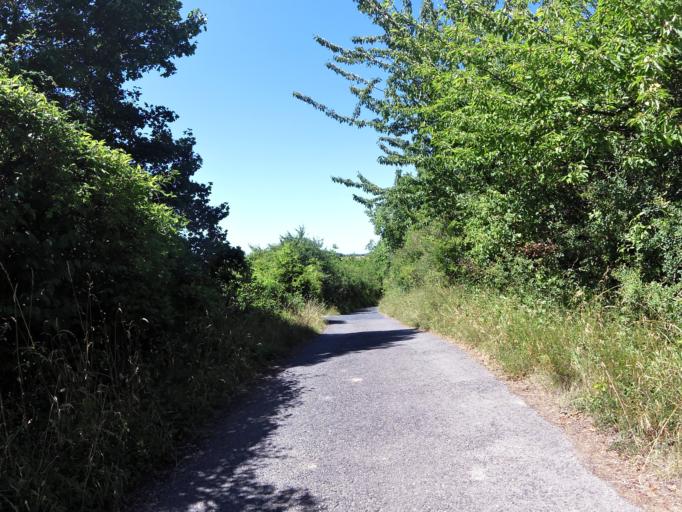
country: DE
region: Bavaria
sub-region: Regierungsbezirk Unterfranken
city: Gerbrunn
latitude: 49.7639
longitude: 9.9966
